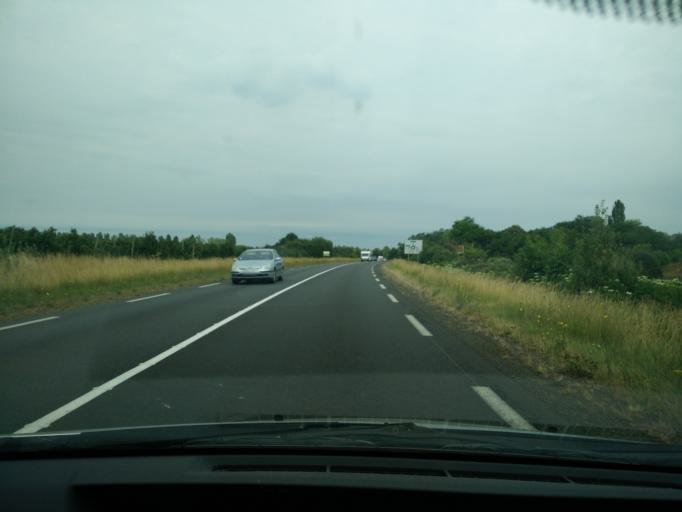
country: FR
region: Pays de la Loire
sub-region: Departement de Maine-et-Loire
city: Doue-la-Fontaine
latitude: 47.1862
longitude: -0.2986
